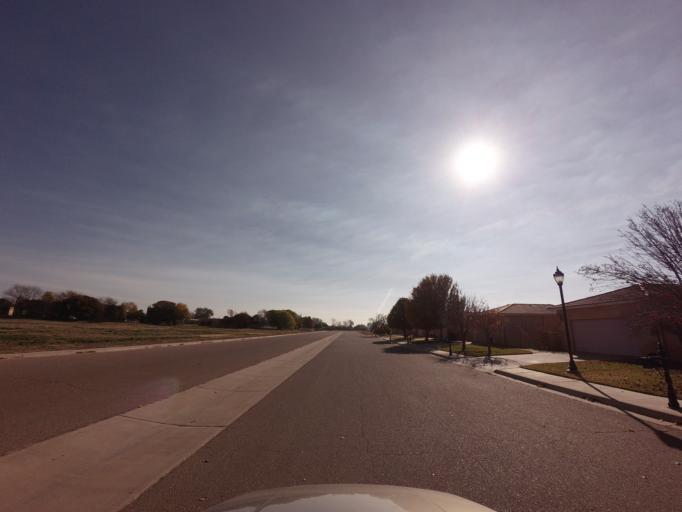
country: US
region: New Mexico
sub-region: Curry County
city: Clovis
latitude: 34.4072
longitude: -103.1774
